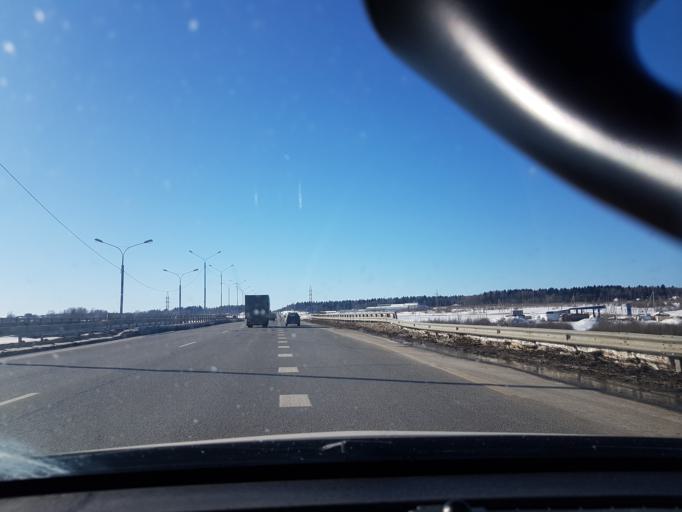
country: RU
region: Moskovskaya
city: Sychevo
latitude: 55.9942
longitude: 36.2345
